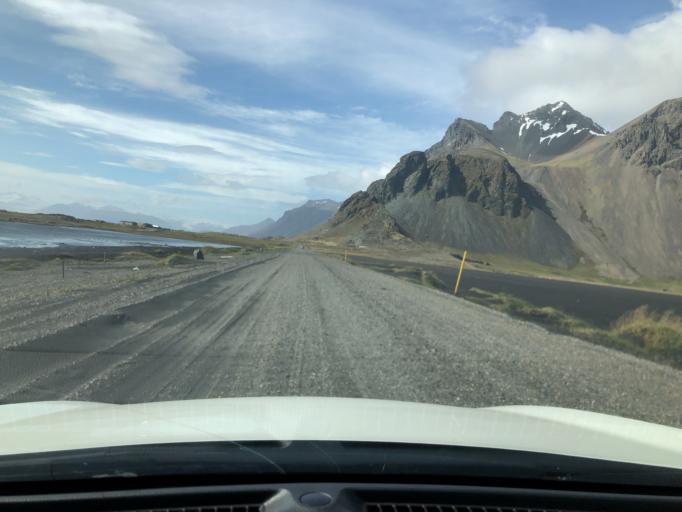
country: IS
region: East
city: Hoefn
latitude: 64.2490
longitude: -14.9823
